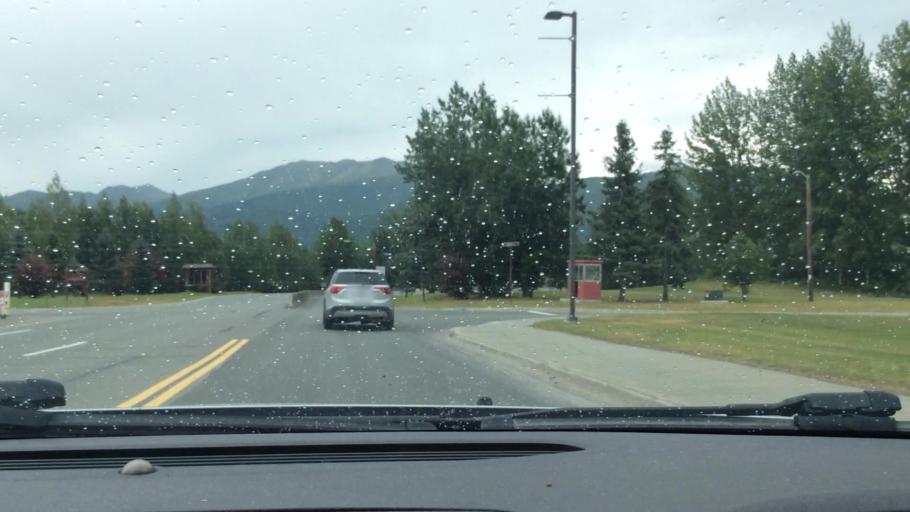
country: US
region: Alaska
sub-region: Anchorage Municipality
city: Elmendorf Air Force Base
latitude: 61.2580
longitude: -149.6710
